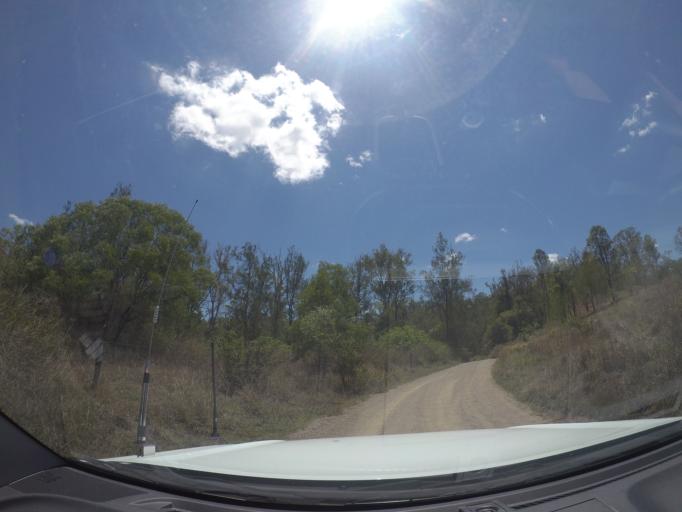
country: AU
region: Queensland
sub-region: Ipswich
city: Springfield Lakes
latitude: -27.8124
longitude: 152.8502
